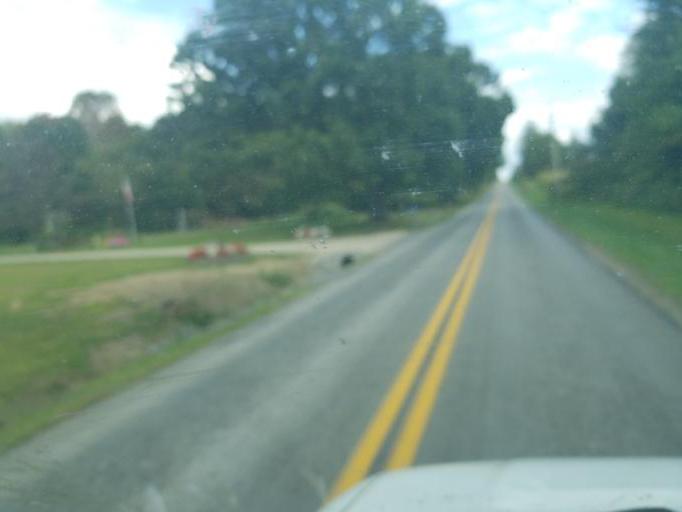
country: US
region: Pennsylvania
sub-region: Crawford County
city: Conneaut Lakeshore
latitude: 41.5247
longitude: -80.3353
